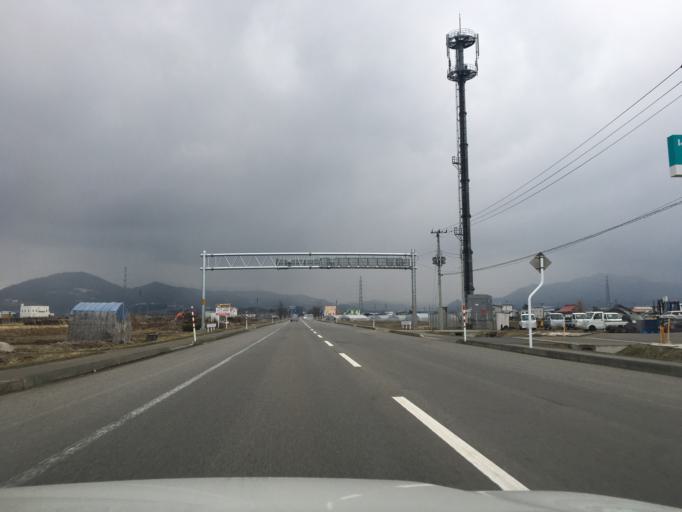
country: JP
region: Aomori
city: Kuroishi
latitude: 40.5796
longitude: 140.5685
